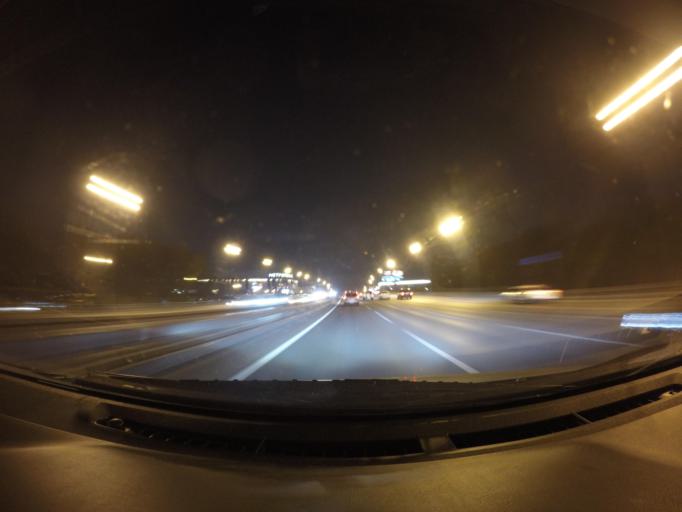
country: RU
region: Moskovskaya
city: Levoberezhnyy
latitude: 55.8266
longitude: 37.4916
